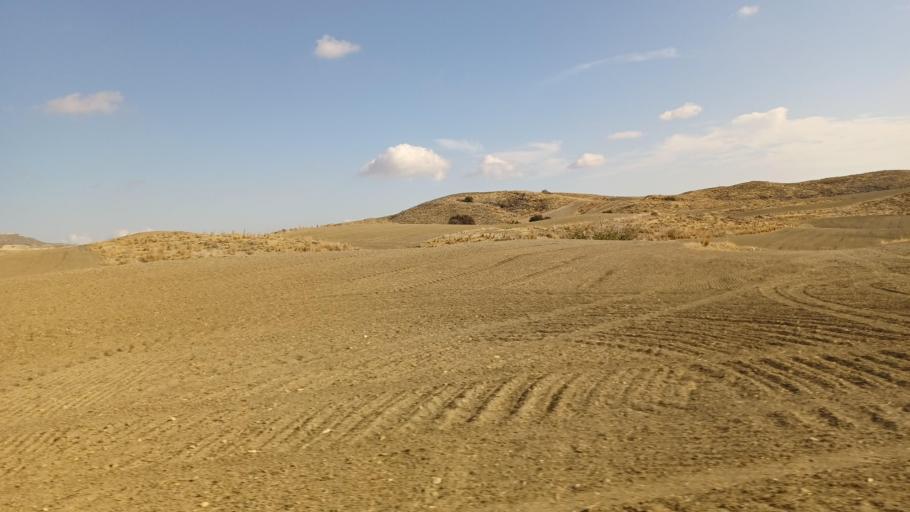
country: CY
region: Larnaka
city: Troulloi
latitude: 35.0225
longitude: 33.5846
